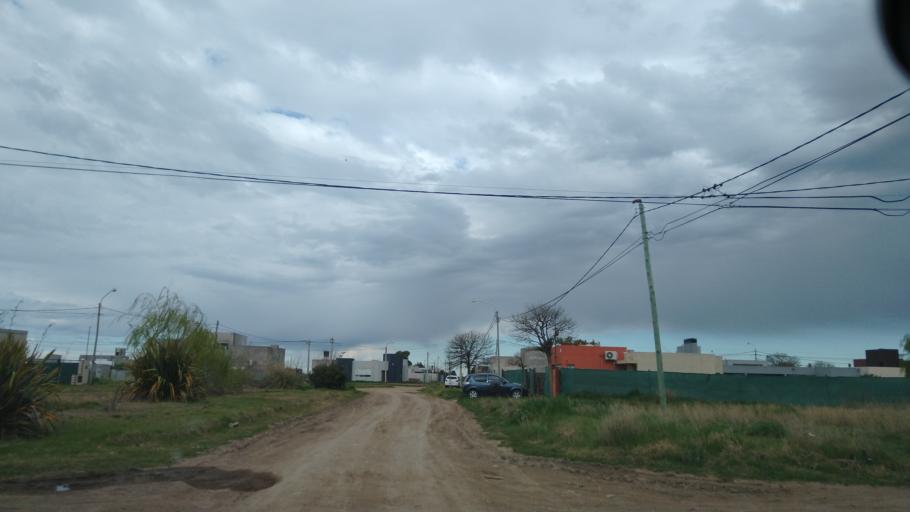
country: AR
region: Buenos Aires
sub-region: Partido de Bahia Blanca
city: Bahia Blanca
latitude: -38.7044
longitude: -62.2009
